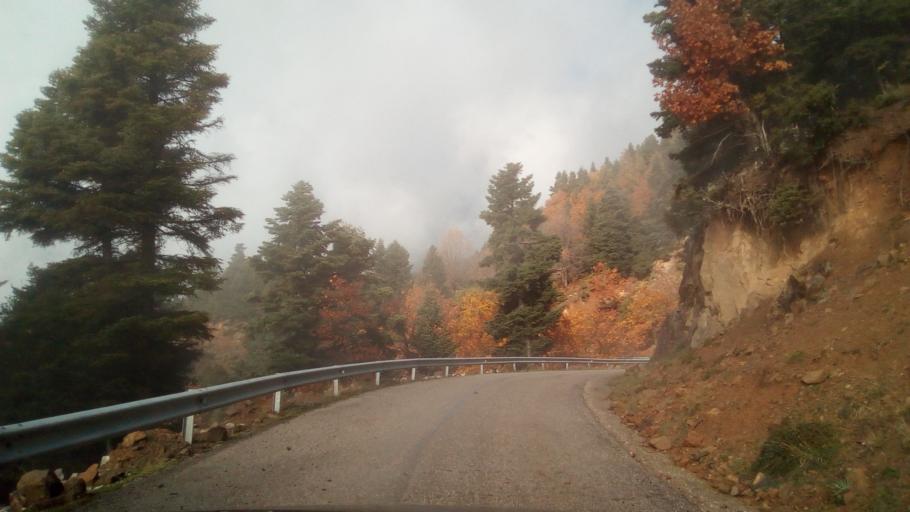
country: GR
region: West Greece
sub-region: Nomos Aitolias kai Akarnanias
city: Nafpaktos
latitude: 38.5651
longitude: 21.9264
